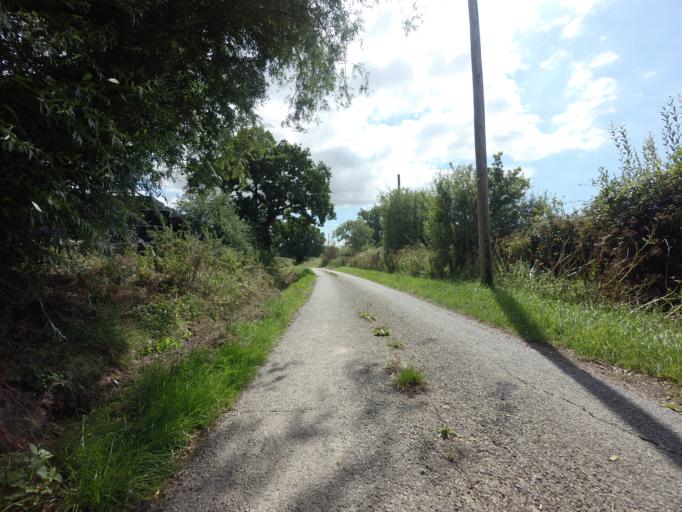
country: GB
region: England
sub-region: Kent
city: Stone
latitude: 51.0469
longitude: 0.7763
